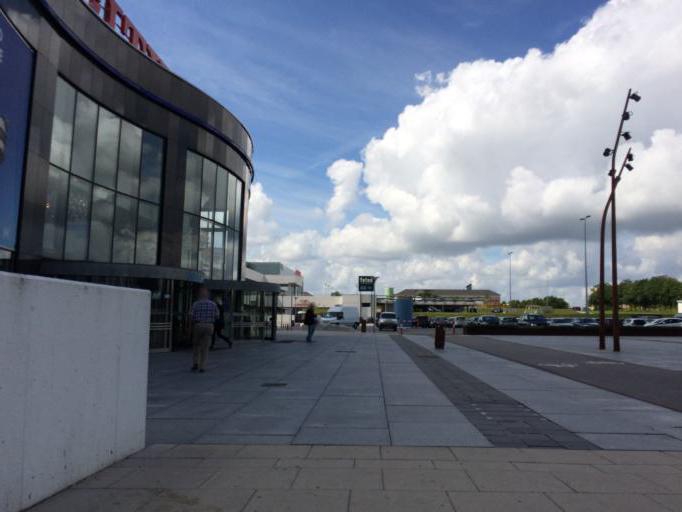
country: DK
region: Capital Region
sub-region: Hoje-Taastrup Kommune
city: Taastrup
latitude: 55.6447
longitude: 12.2781
